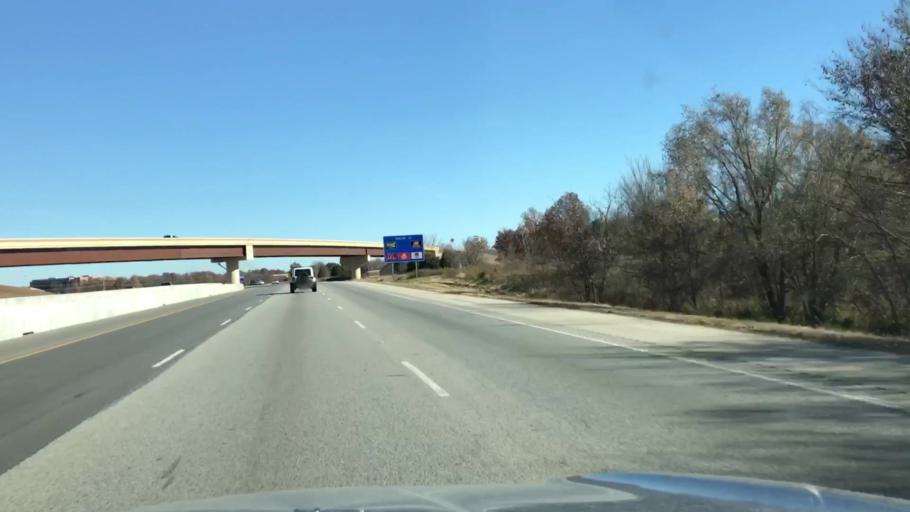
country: US
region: Arkansas
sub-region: Benton County
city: Lowell
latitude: 36.2376
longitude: -94.1602
